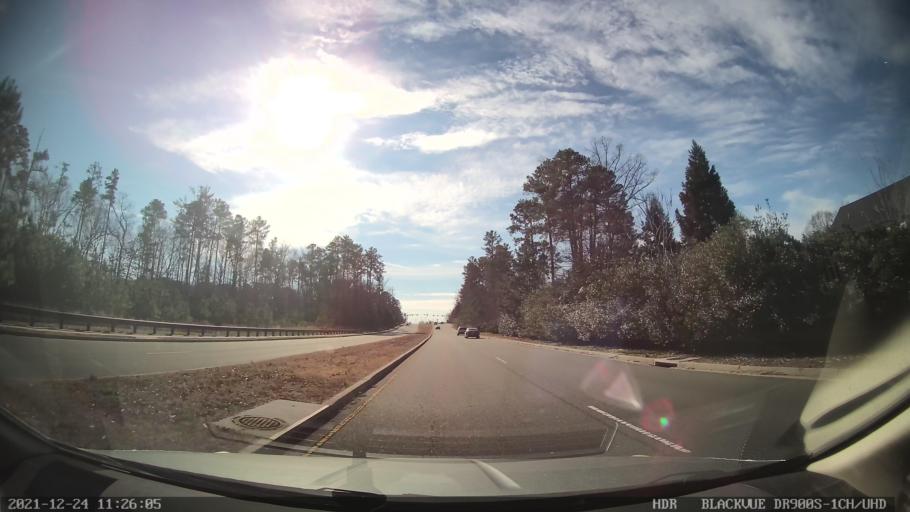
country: US
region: Virginia
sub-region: Henrico County
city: Short Pump
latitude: 37.6387
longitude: -77.6126
